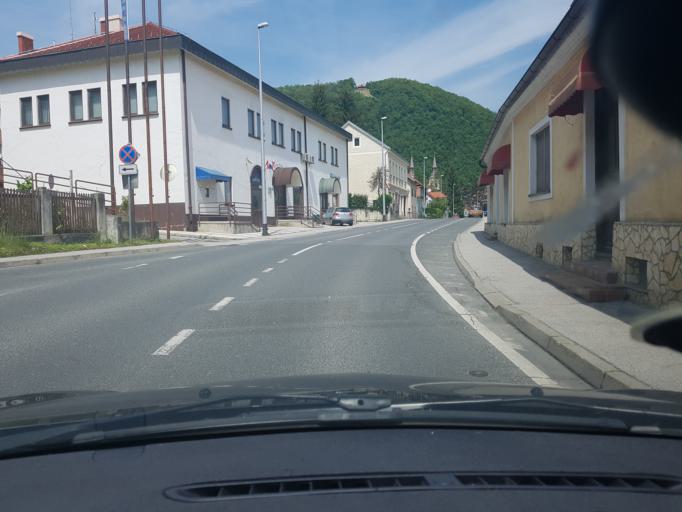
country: HR
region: Krapinsko-Zagorska
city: Pregrada
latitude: 46.1614
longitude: 15.7499
